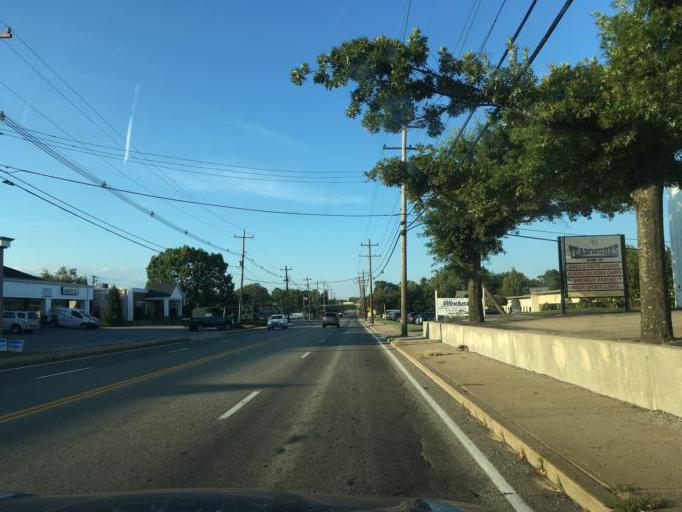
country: US
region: Rhode Island
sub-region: Providence County
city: Cranston
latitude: 41.7438
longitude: -71.4375
